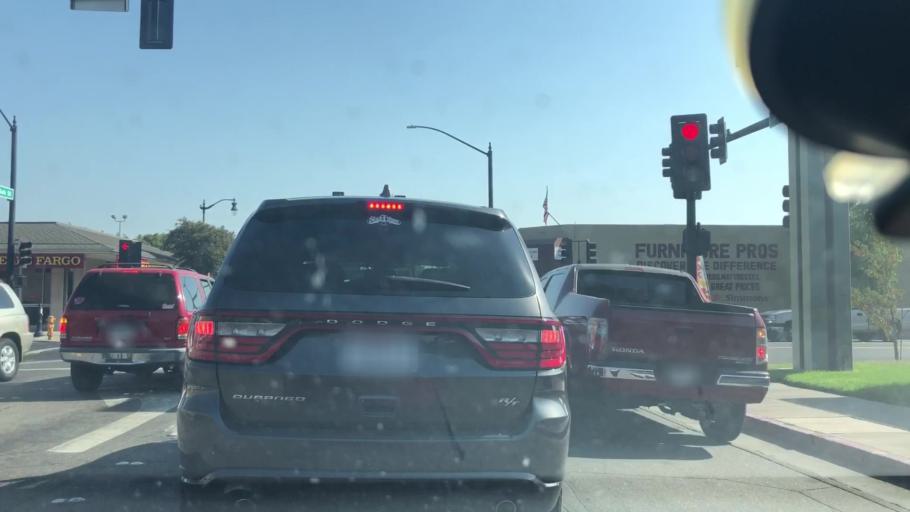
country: US
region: California
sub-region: San Joaquin County
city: Manteca
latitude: 37.7994
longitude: -121.2166
